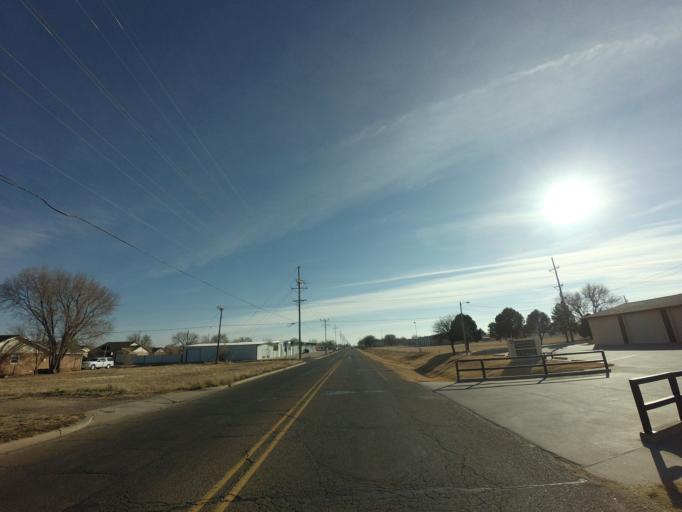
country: US
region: New Mexico
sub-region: Curry County
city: Clovis
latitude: 34.4124
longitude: -103.2317
